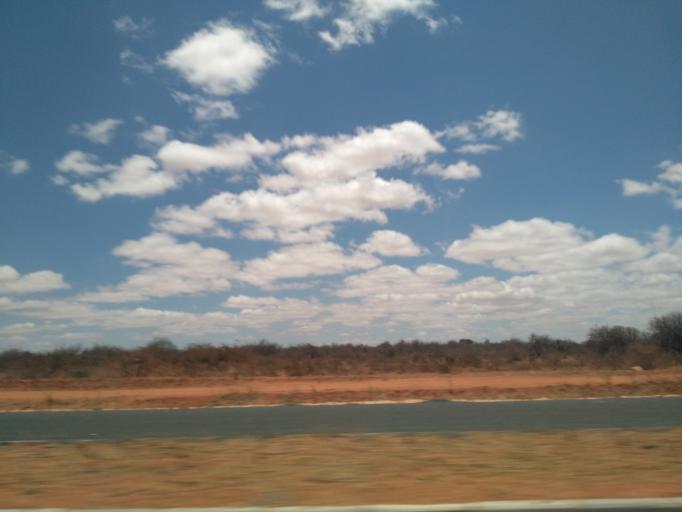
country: TZ
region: Dodoma
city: Kisasa
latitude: -6.1699
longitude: 35.8405
